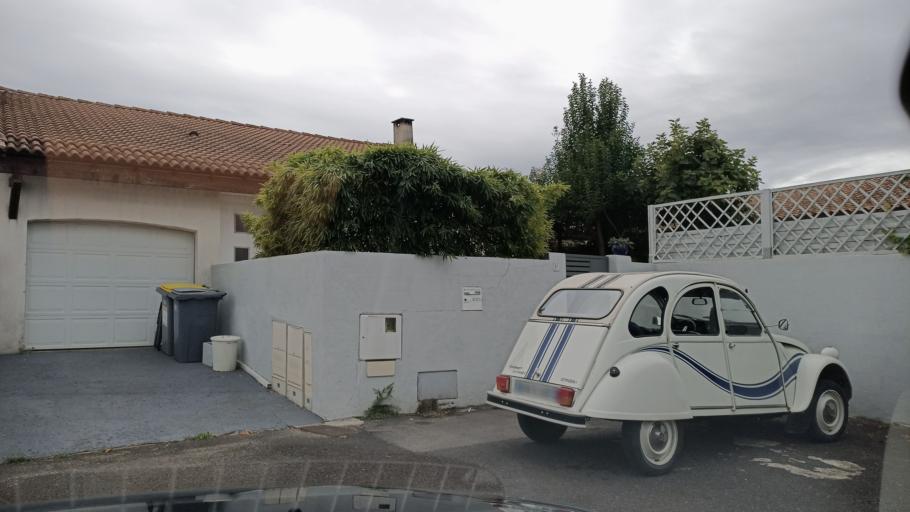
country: FR
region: Languedoc-Roussillon
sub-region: Departement de l'Herault
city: Lunel
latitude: 43.6858
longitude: 4.1408
